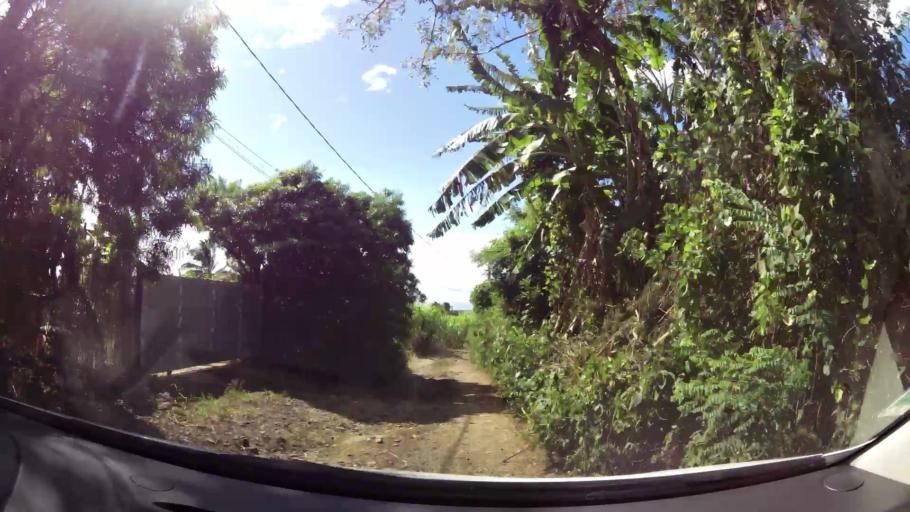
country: RE
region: Reunion
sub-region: Reunion
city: Sainte-Marie
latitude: -20.9240
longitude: 55.5056
